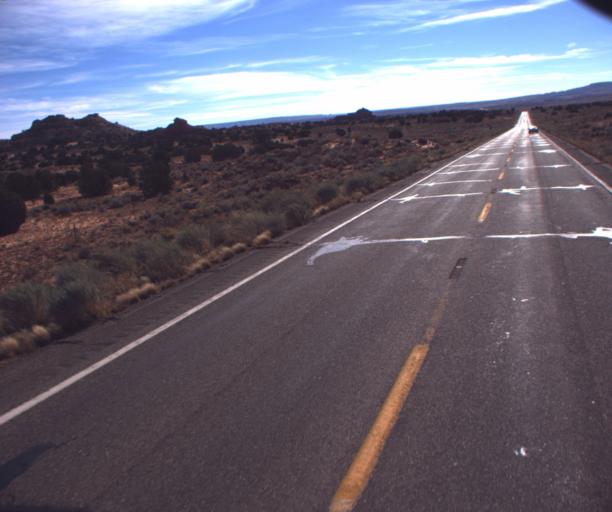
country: US
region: Arizona
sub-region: Coconino County
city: Kaibito
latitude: 36.6374
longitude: -111.2144
